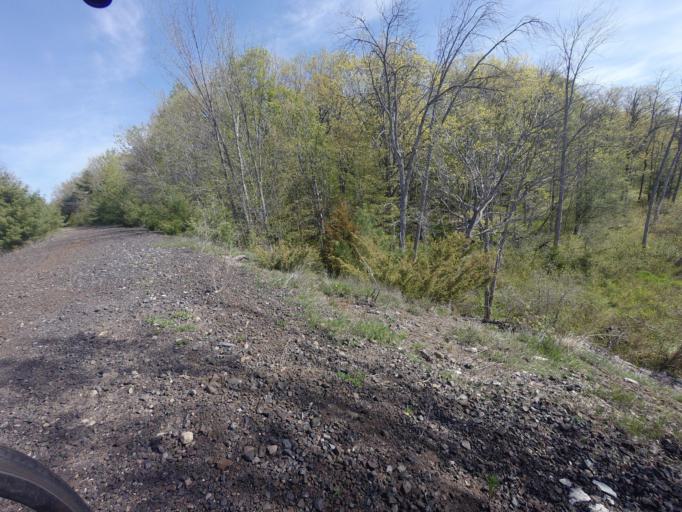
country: CA
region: Ontario
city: Arnprior
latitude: 45.4686
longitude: -76.2872
